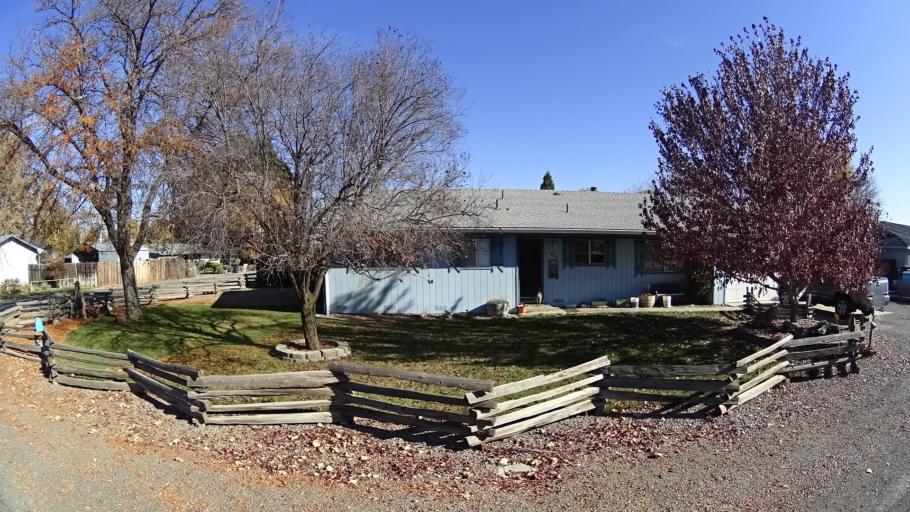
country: US
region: California
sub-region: Siskiyou County
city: Montague
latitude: 41.6438
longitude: -122.5250
